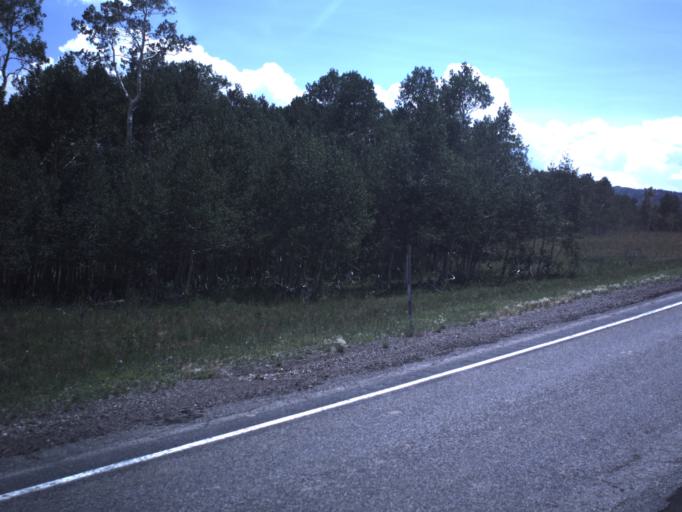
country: US
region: Utah
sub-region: Sanpete County
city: Fairview
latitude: 39.6634
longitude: -111.3290
